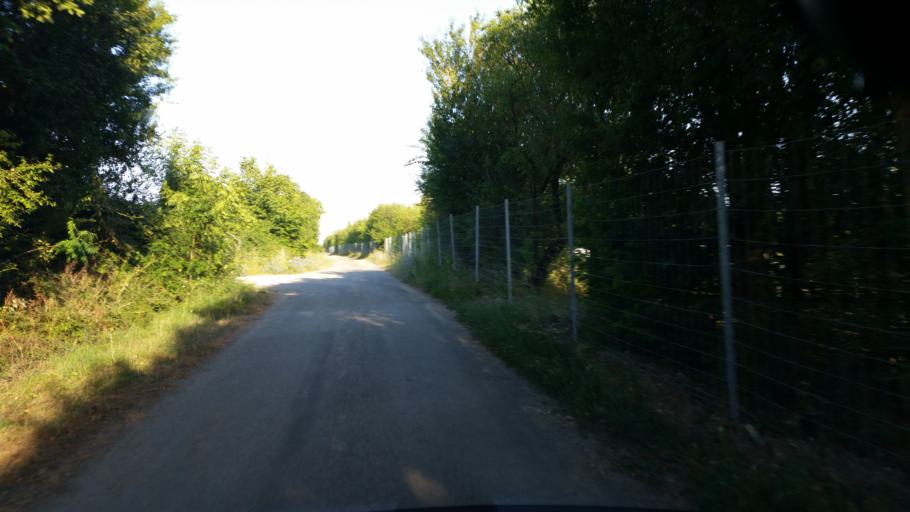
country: FR
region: Poitou-Charentes
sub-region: Departement de la Charente-Maritime
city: Saint-Jean-de-Liversay
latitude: 46.2266
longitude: -0.8811
